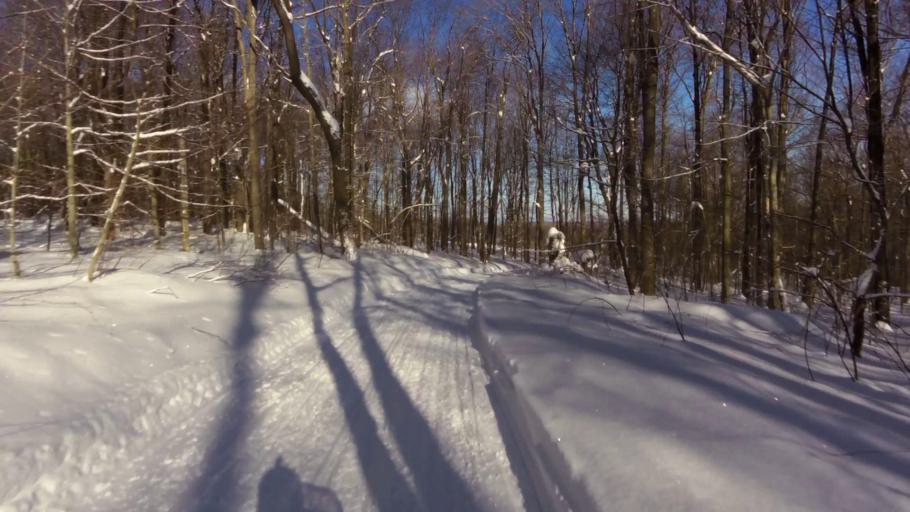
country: US
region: New York
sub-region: Chautauqua County
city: Falconer
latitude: 42.2766
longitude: -79.1259
